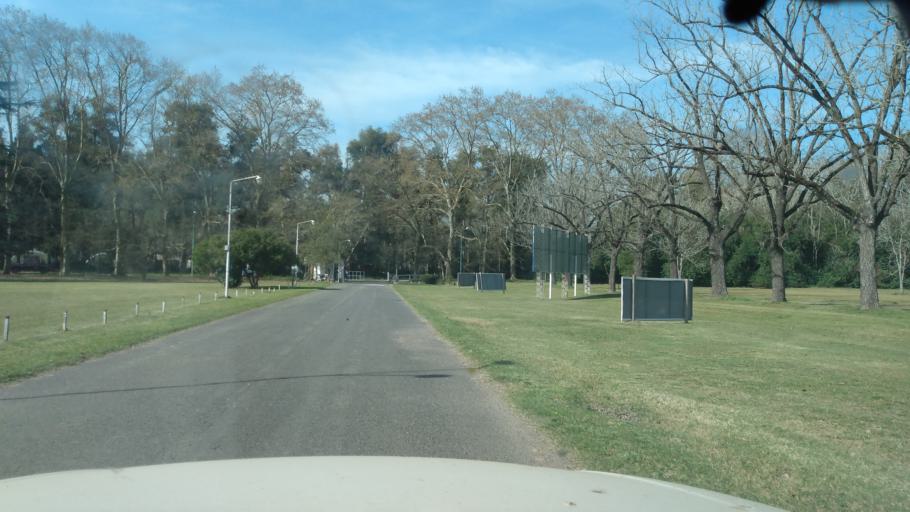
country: AR
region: Buenos Aires
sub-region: Partido de Lujan
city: Lujan
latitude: -34.5921
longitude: -59.1826
